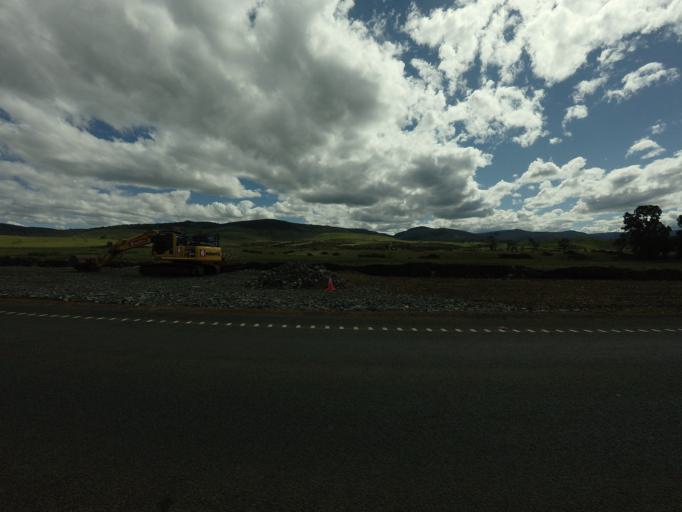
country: AU
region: Tasmania
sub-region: Brighton
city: Bridgewater
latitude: -42.1930
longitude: 147.3905
